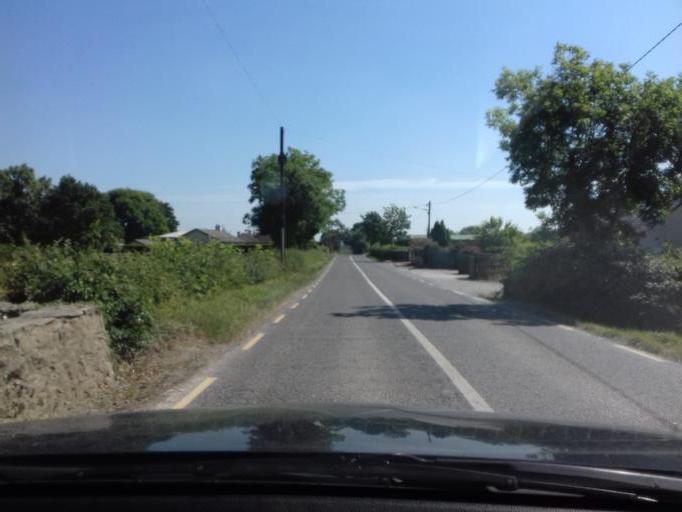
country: IE
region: Leinster
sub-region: Fingal County
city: Swords
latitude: 53.5286
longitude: -6.2688
